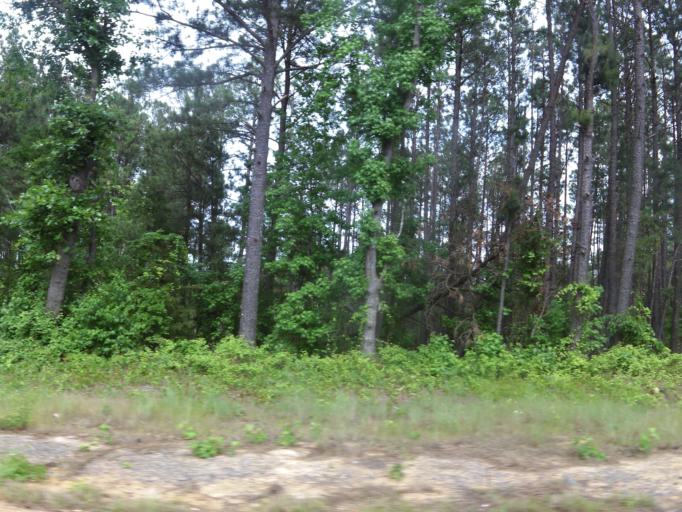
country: US
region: Georgia
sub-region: Jefferson County
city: Wrens
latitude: 33.3265
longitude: -82.4533
